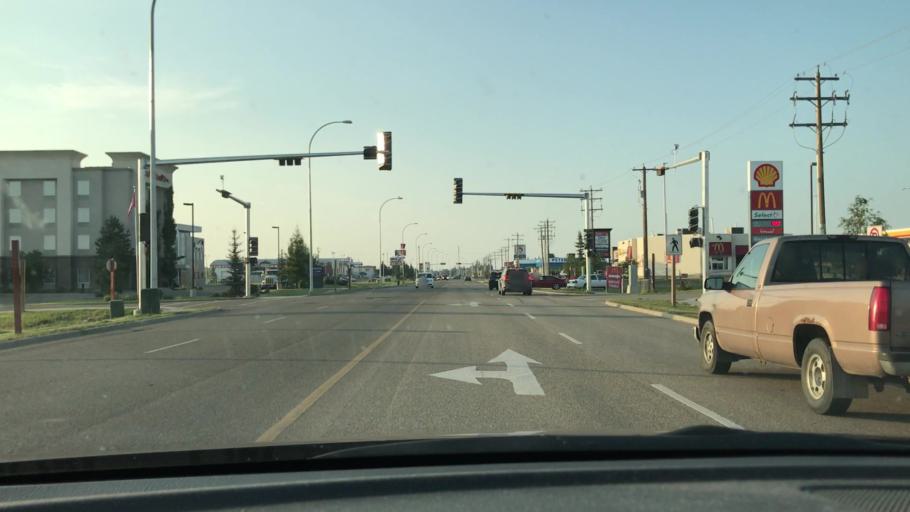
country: CA
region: Alberta
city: Red Deer
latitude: 52.2057
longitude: -113.8162
